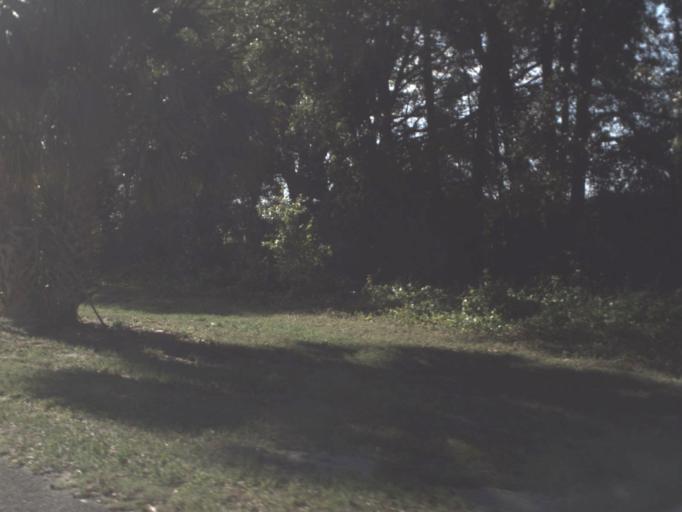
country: US
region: Florida
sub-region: Lake County
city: Mount Plymouth
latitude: 28.8185
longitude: -81.4861
